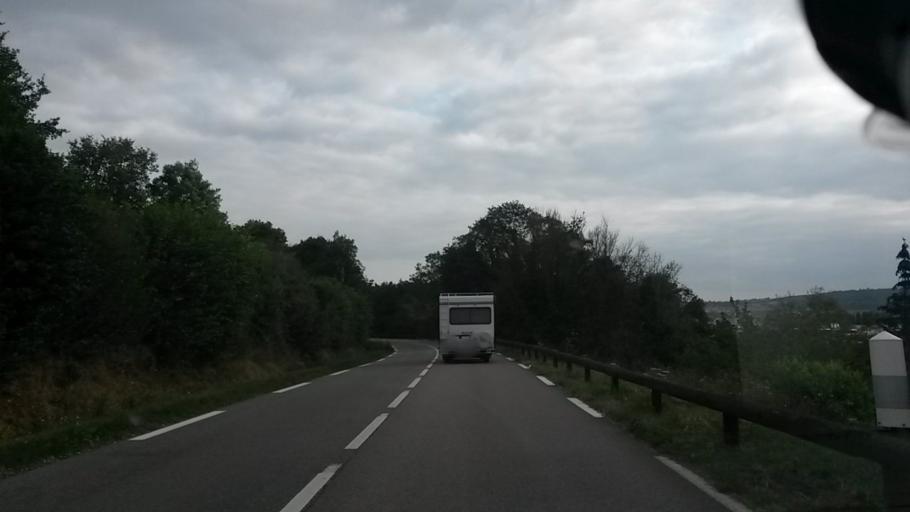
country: FR
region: Haute-Normandie
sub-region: Departement de l'Eure
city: Gravigny
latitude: 49.0657
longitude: 1.1743
